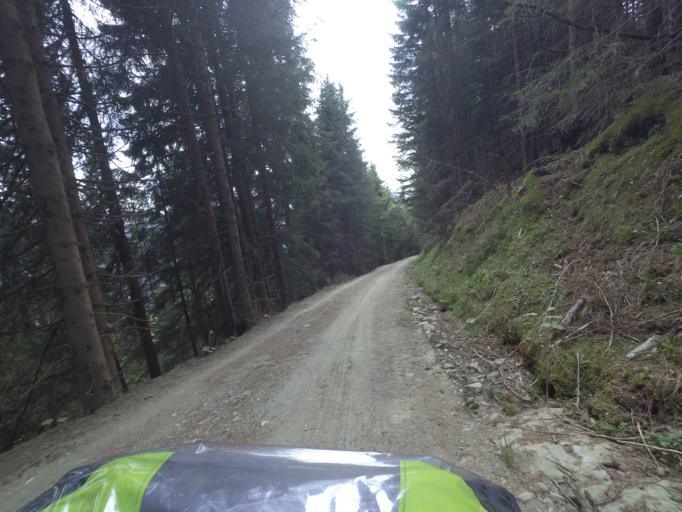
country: AT
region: Salzburg
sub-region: Politischer Bezirk Sankt Johann im Pongau
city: Dorfgastein
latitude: 47.2607
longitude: 13.1248
